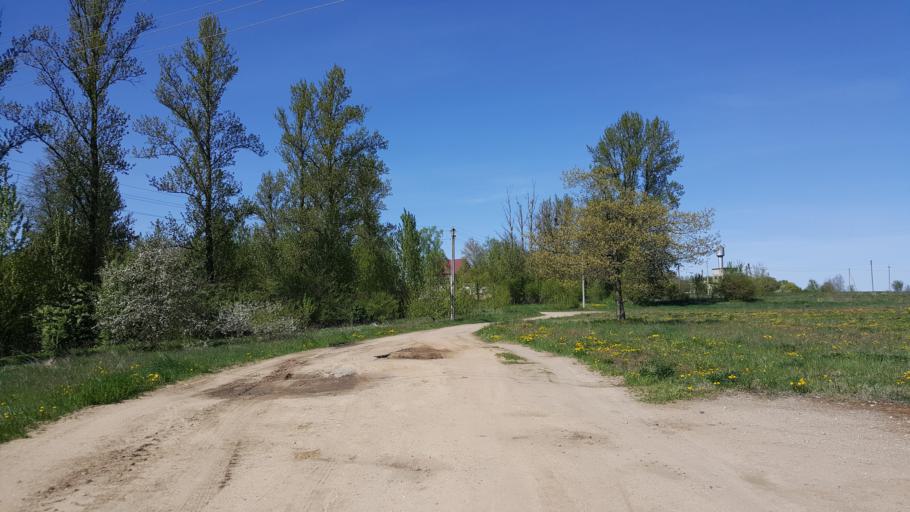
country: BY
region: Brest
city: Kamyanyets
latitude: 52.4389
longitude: 23.8483
